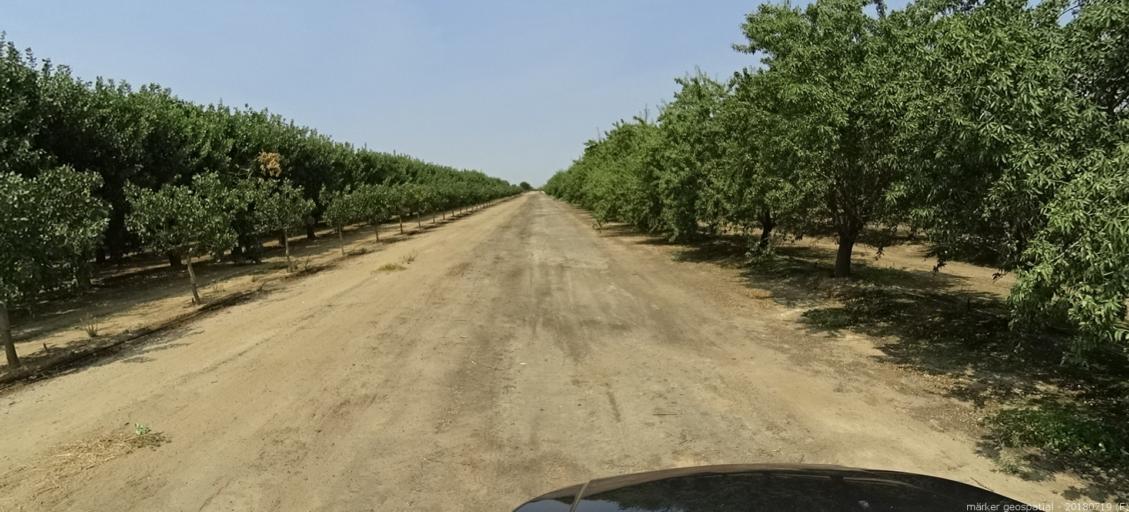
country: US
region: California
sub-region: Madera County
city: Fairmead
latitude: 37.1055
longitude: -120.1860
